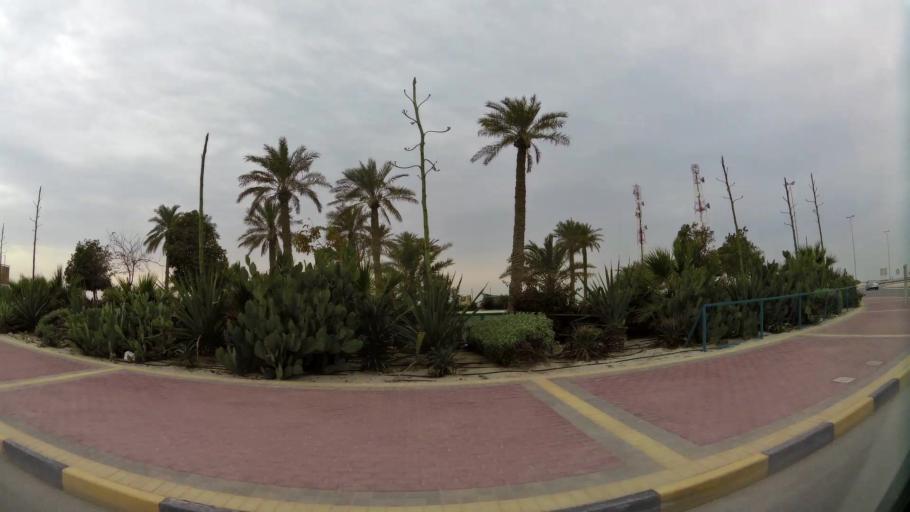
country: BH
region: Central Governorate
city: Dar Kulayb
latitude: 25.8462
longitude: 50.5855
